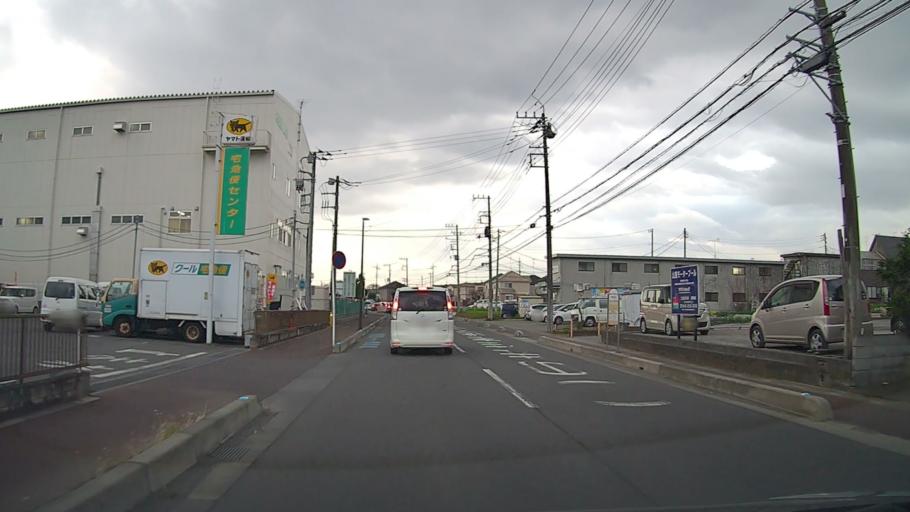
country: JP
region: Saitama
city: Oi
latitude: 35.8595
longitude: 139.5459
